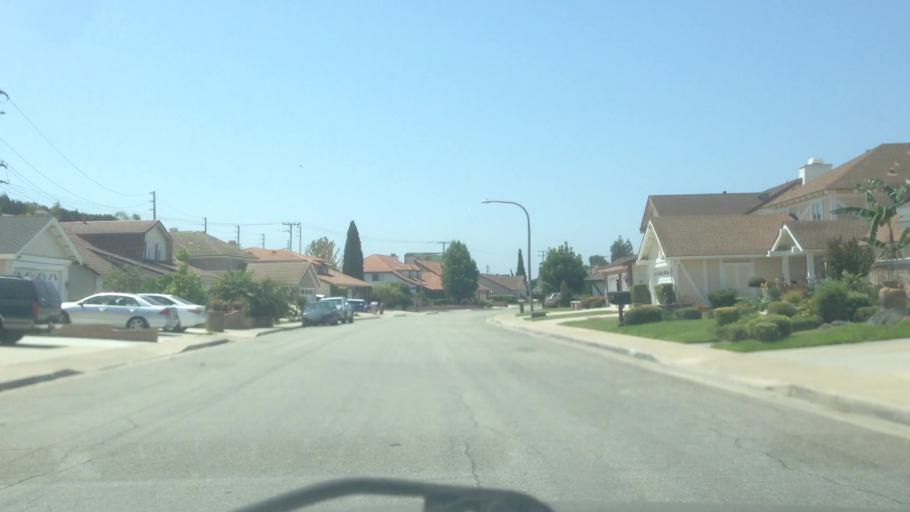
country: US
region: California
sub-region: Orange County
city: Fountain Valley
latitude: 33.7227
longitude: -117.9204
